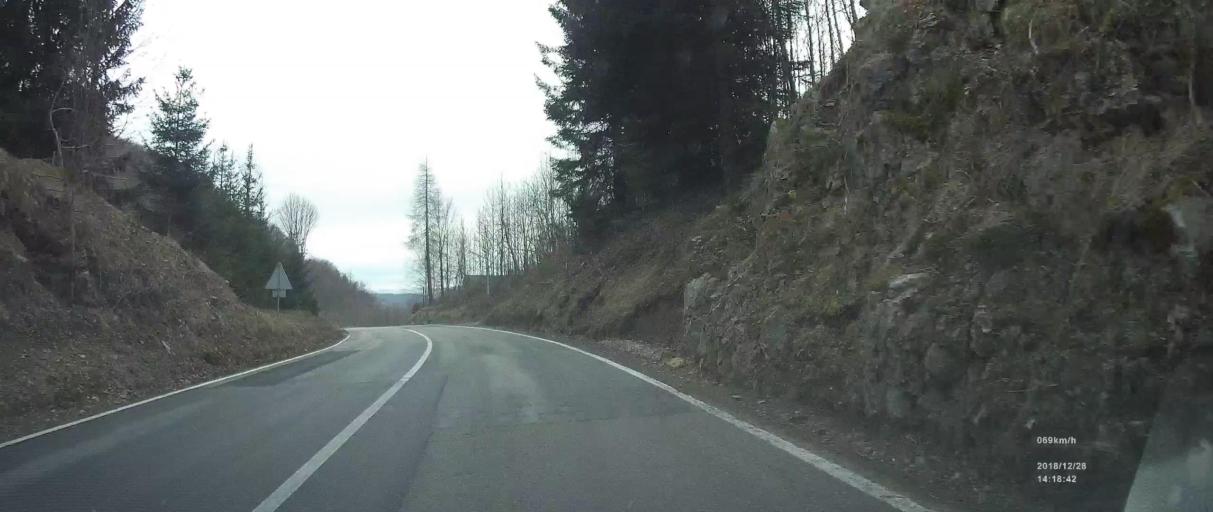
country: HR
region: Primorsko-Goranska
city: Vrbovsko
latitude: 45.4100
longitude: 15.0605
